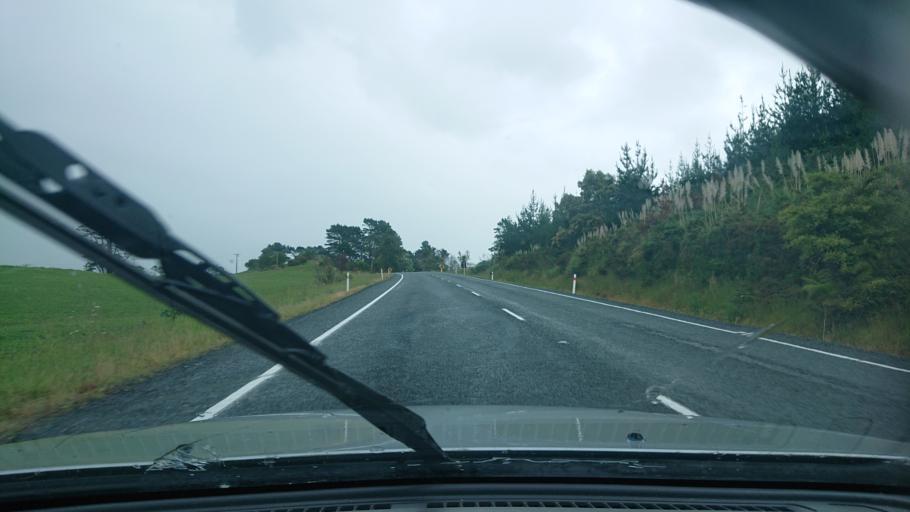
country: NZ
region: Auckland
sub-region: Auckland
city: Wellsford
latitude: -36.3308
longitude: 174.4695
